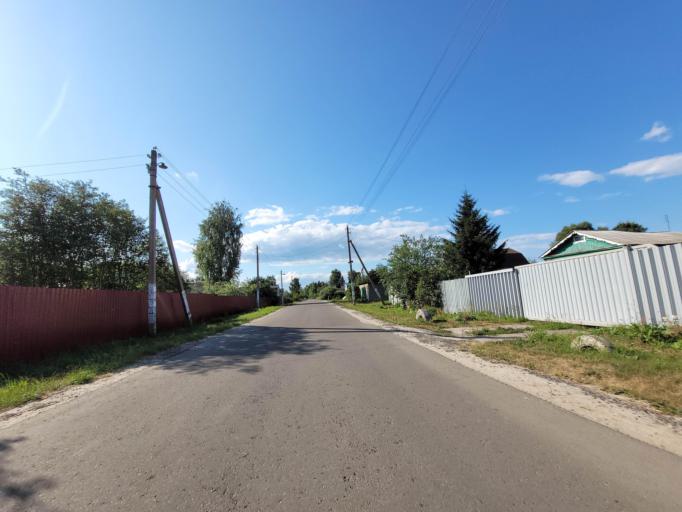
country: RU
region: Moskovskaya
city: Konobeyevo
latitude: 55.4074
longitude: 38.7027
